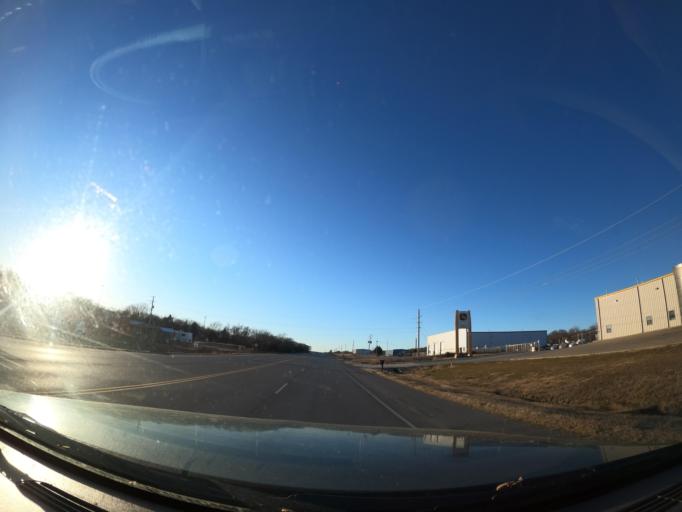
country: US
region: Oklahoma
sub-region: Pittsburg County
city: Krebs
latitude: 34.8970
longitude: -95.6754
